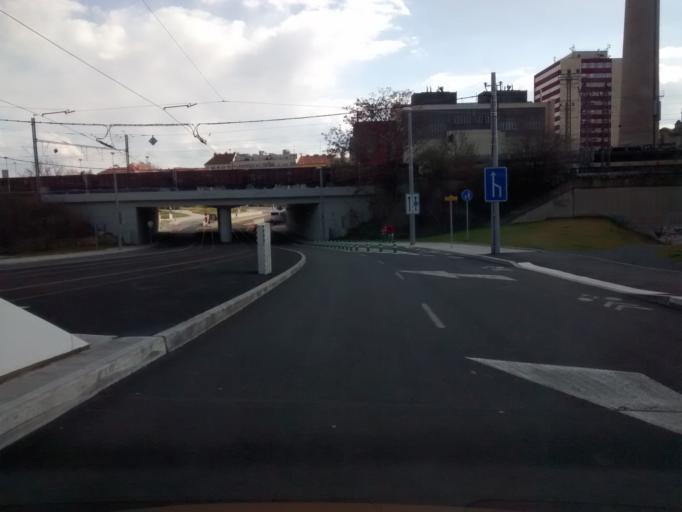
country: CZ
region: Praha
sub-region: Praha 8
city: Karlin
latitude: 50.1114
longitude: 14.4364
